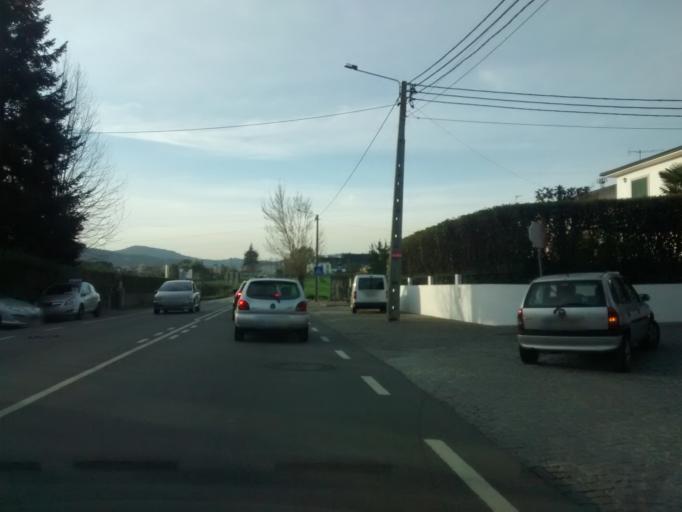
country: PT
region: Braga
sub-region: Guimaraes
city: Ponte
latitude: 41.4710
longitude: -8.3298
